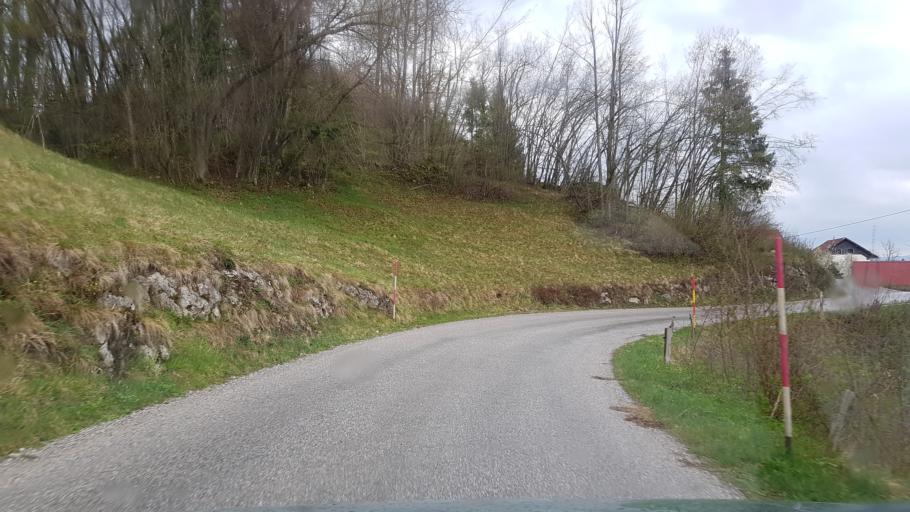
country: SI
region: Cerkno
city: Cerkno
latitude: 46.1144
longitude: 13.8531
